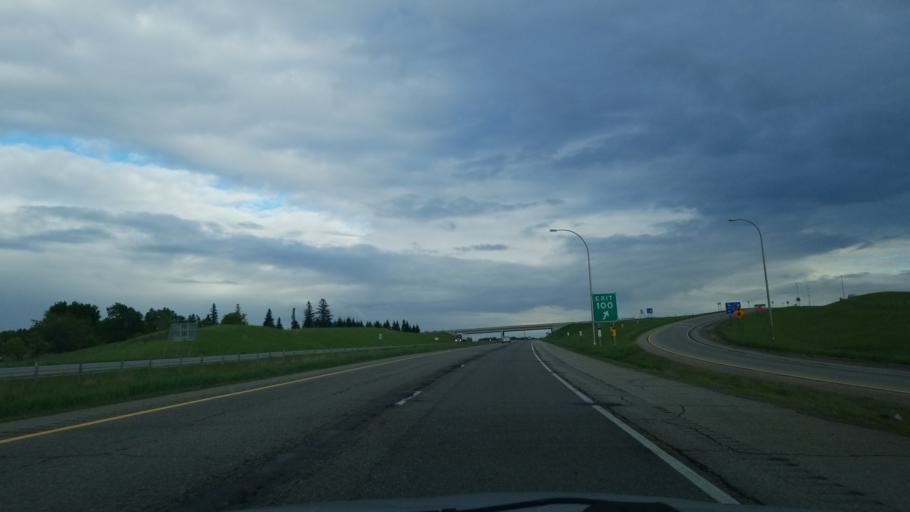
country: US
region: Minnesota
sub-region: Douglas County
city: Alexandria
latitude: 45.8631
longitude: -95.4332
